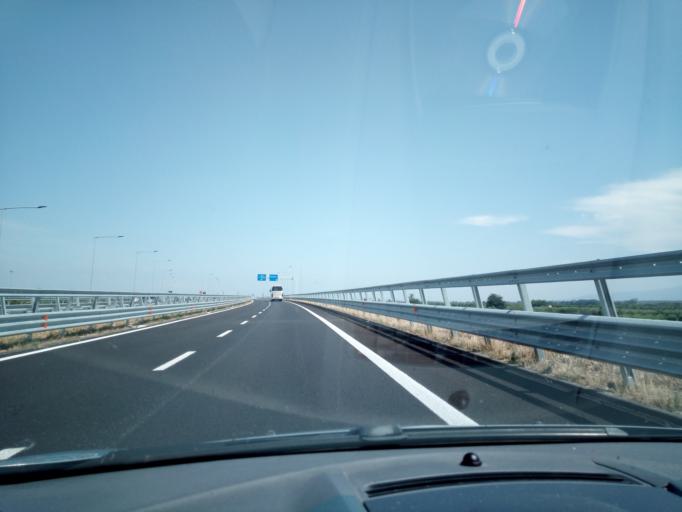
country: IT
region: Calabria
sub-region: Provincia di Cosenza
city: Doria
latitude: 39.7235
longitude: 16.3617
